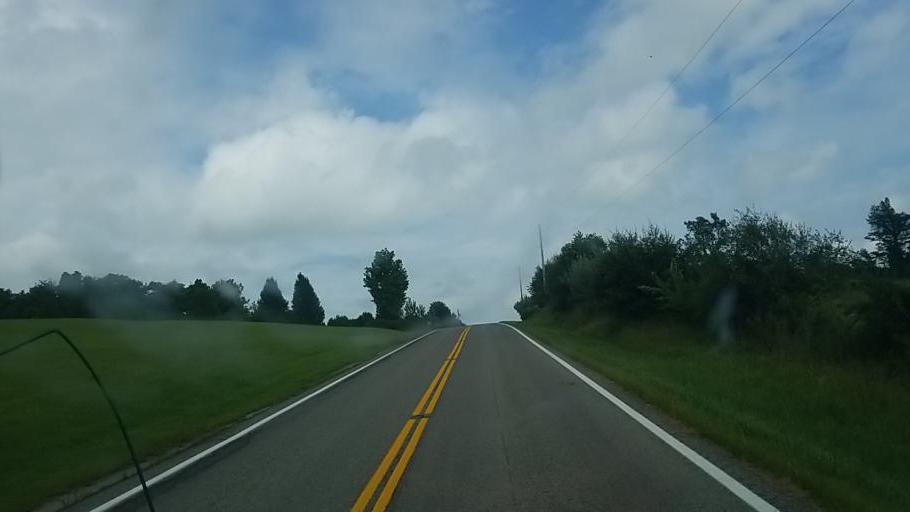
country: US
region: Ohio
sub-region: Champaign County
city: North Lewisburg
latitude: 40.2592
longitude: -83.6509
